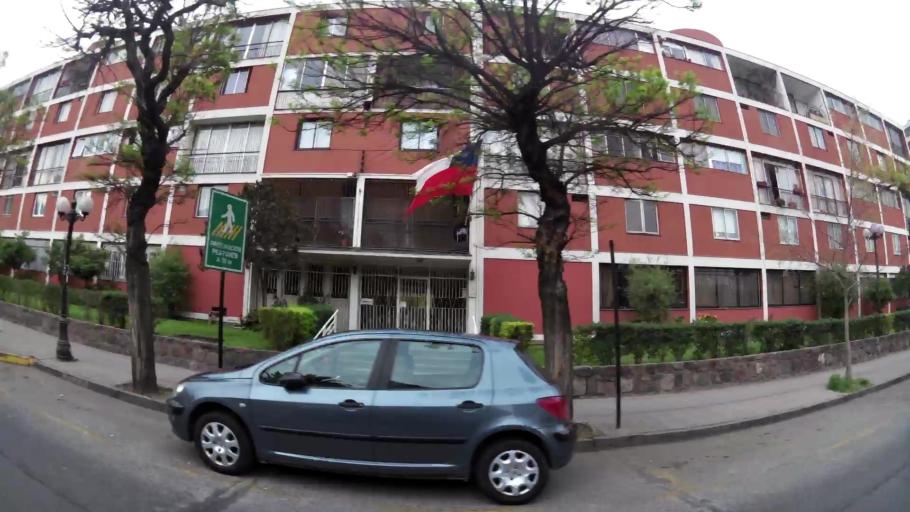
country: CL
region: Santiago Metropolitan
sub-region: Provincia de Santiago
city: Santiago
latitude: -33.4303
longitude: -70.6167
